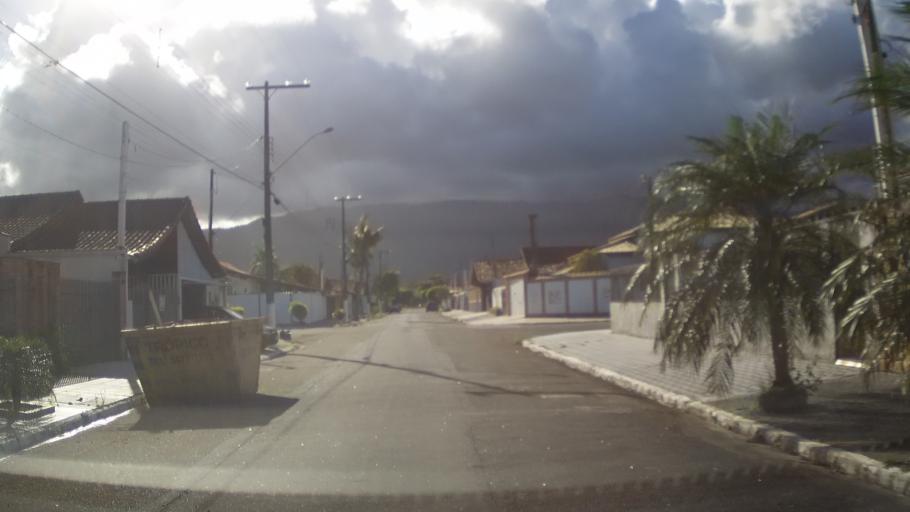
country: BR
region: Sao Paulo
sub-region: Mongagua
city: Mongagua
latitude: -24.0581
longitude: -46.5487
